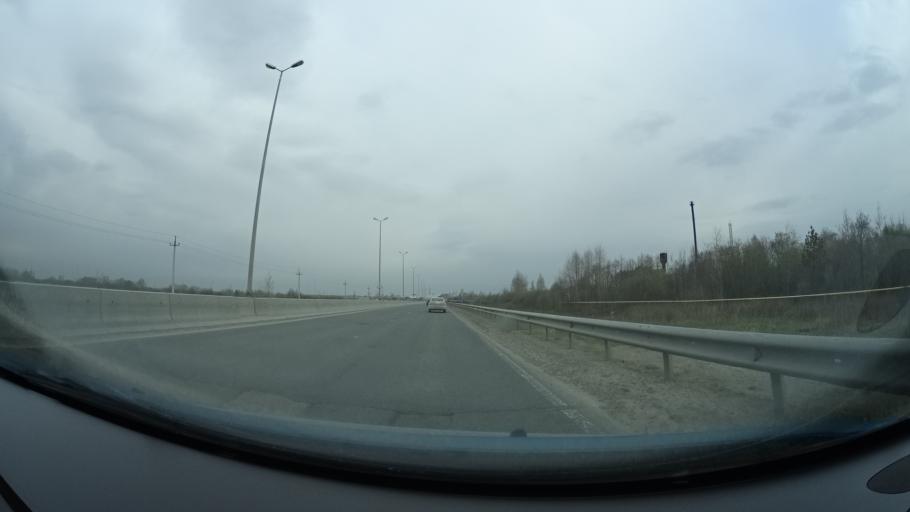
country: RU
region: Perm
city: Kondratovo
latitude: 58.0066
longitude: 56.0655
